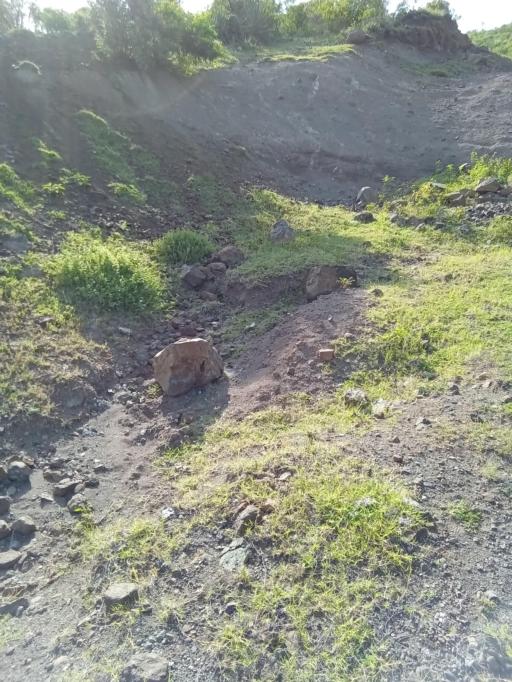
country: KE
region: Homa Bay
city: Homa Bay
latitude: -0.4603
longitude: 34.1987
